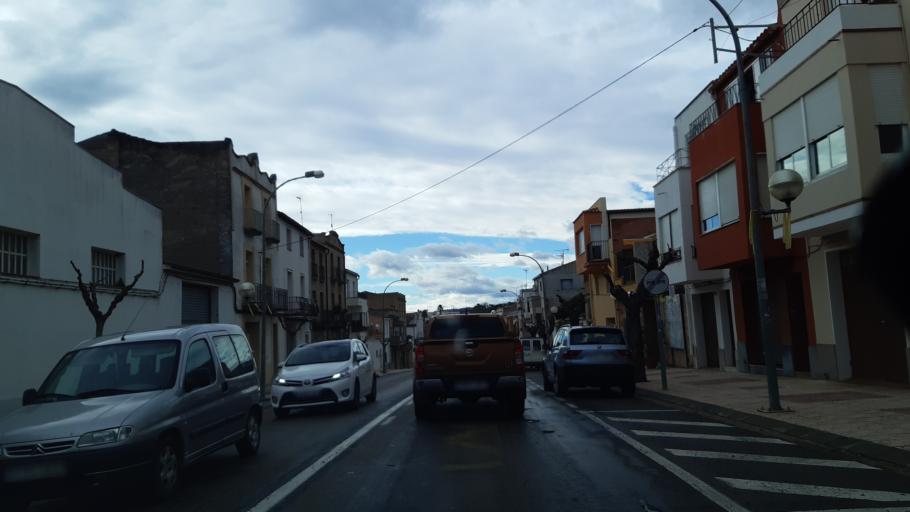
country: ES
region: Catalonia
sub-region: Provincia de Tarragona
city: Gandesa
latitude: 41.0762
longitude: 0.4734
